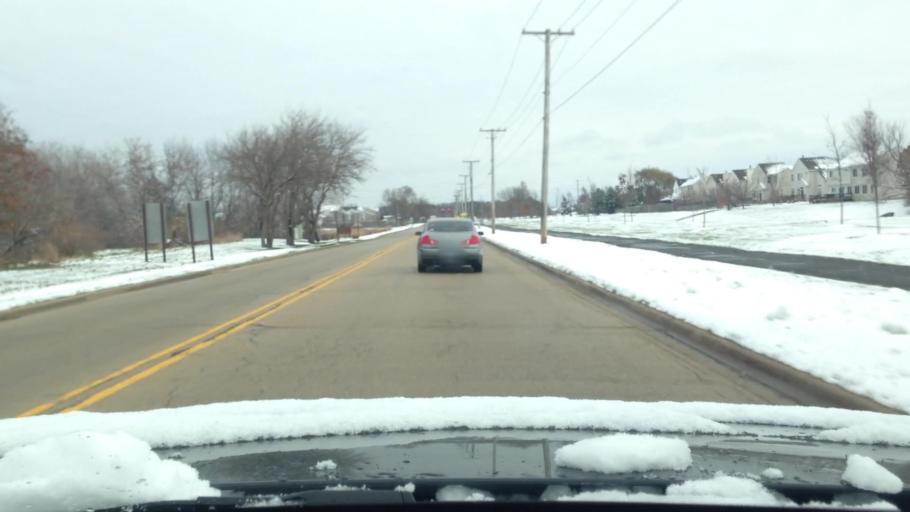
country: US
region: Illinois
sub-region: McHenry County
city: Huntley
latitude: 42.1829
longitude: -88.3899
